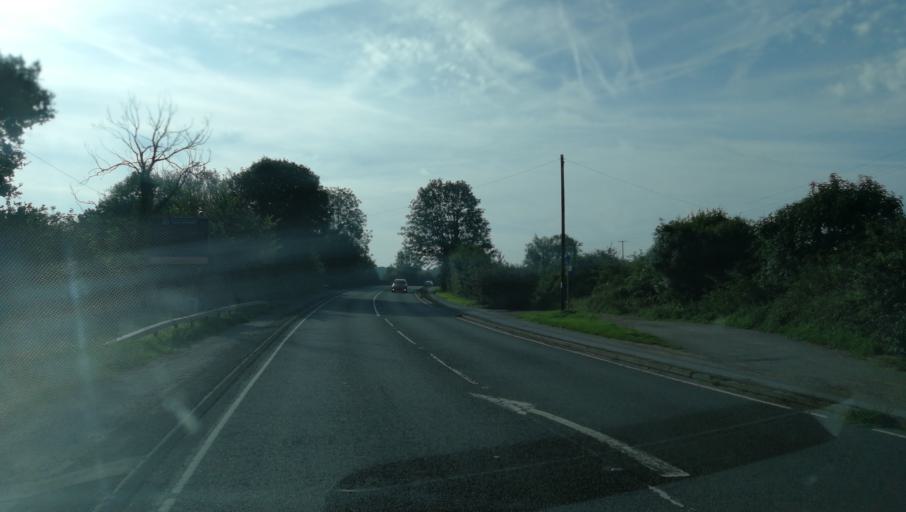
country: GB
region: England
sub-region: Oxfordshire
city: Yarnton
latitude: 51.8016
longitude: -1.2928
